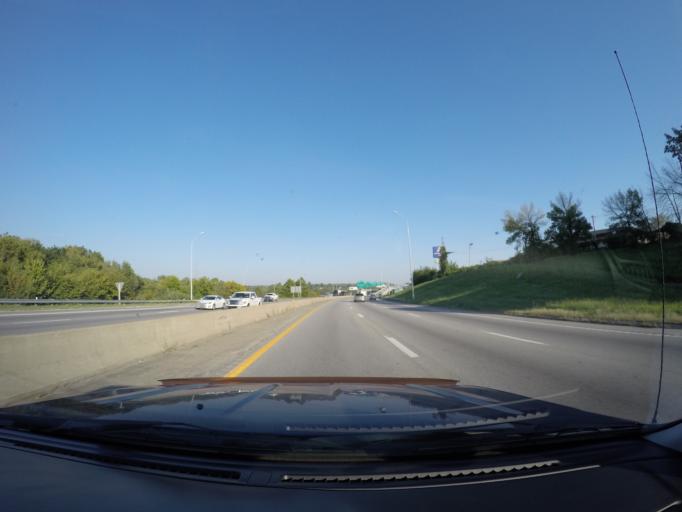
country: US
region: Missouri
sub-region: Jackson County
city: Kansas City
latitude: 39.0699
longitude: -94.5142
